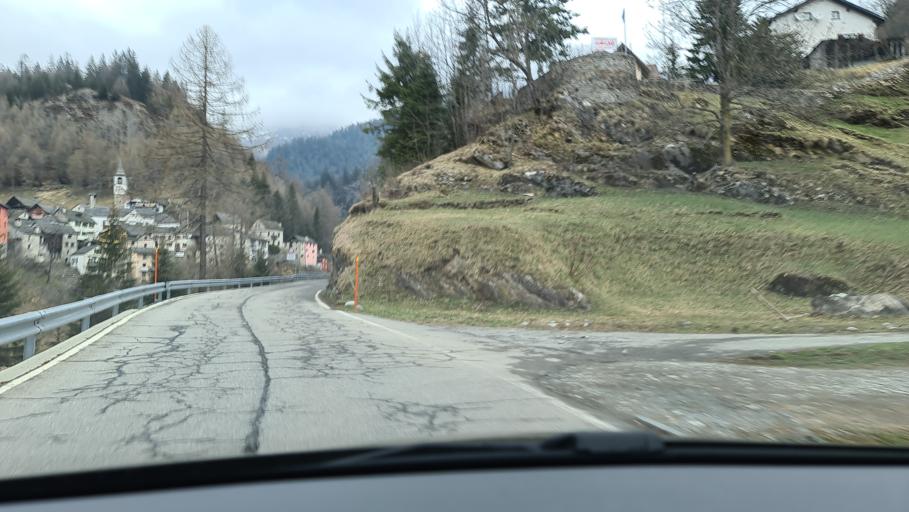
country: CH
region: Ticino
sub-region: Leventina District
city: Airolo
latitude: 46.4415
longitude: 8.6623
